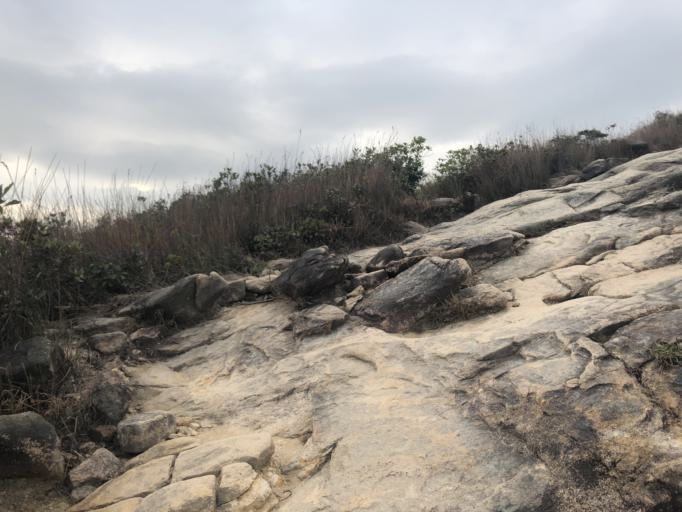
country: HK
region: Wanchai
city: Wan Chai
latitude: 22.2689
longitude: 114.2077
